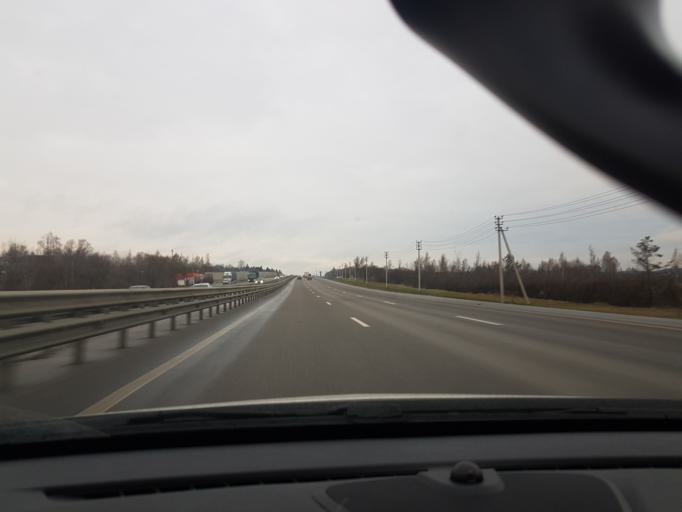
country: RU
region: Moskovskaya
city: Rumyantsevo
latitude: 55.9262
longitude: 36.5732
